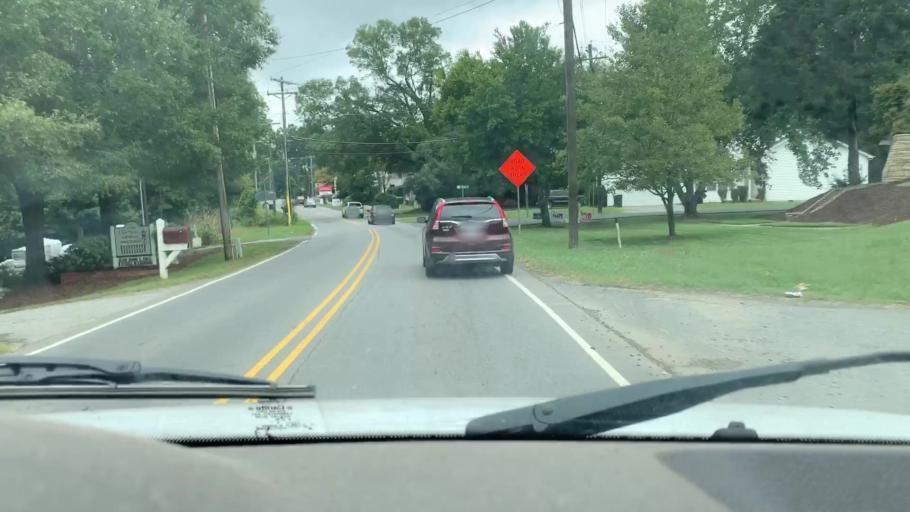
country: US
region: North Carolina
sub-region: Mecklenburg County
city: Huntersville
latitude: 35.4033
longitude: -80.8399
